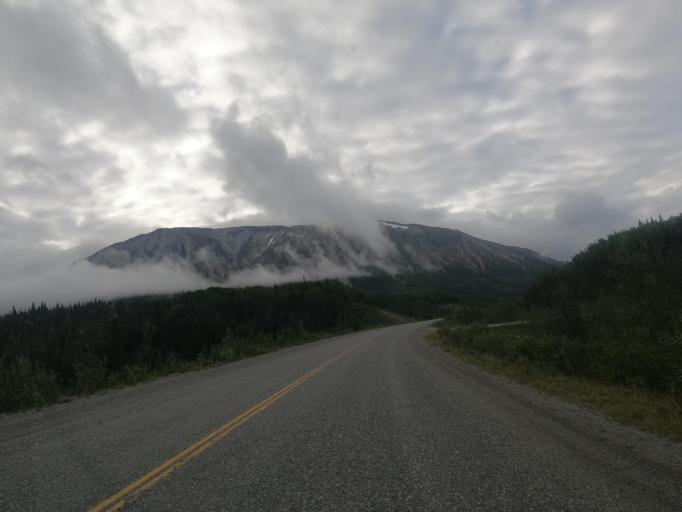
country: CA
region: Yukon
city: Haines Junction
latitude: 60.1106
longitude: -136.9262
